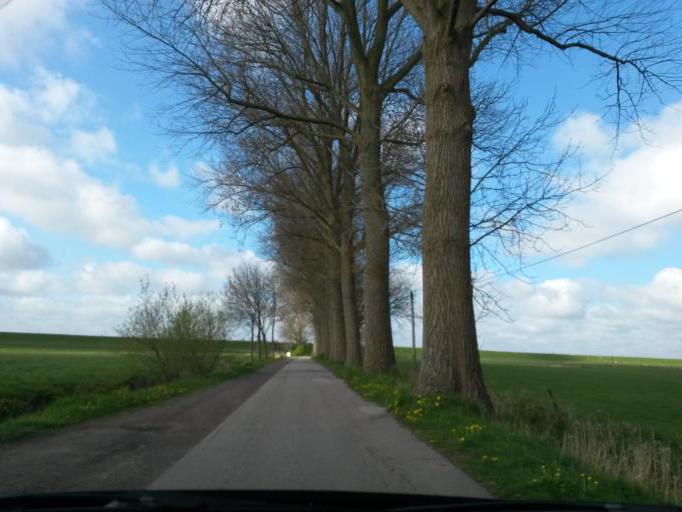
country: DE
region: Schleswig-Holstein
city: Wedel
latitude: 53.5831
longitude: 9.6669
